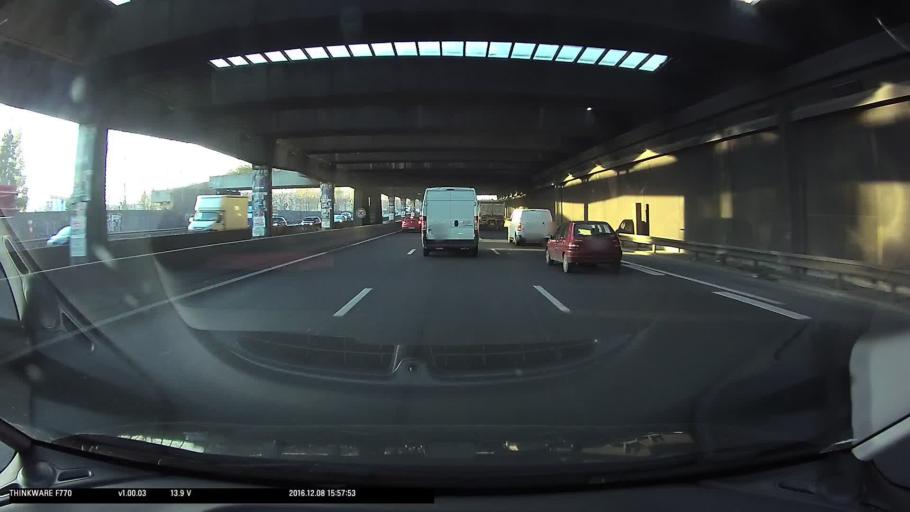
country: FR
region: Ile-de-France
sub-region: Departement des Hauts-de-Seine
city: Villeneuve-la-Garenne
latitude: 48.9298
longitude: 2.3273
